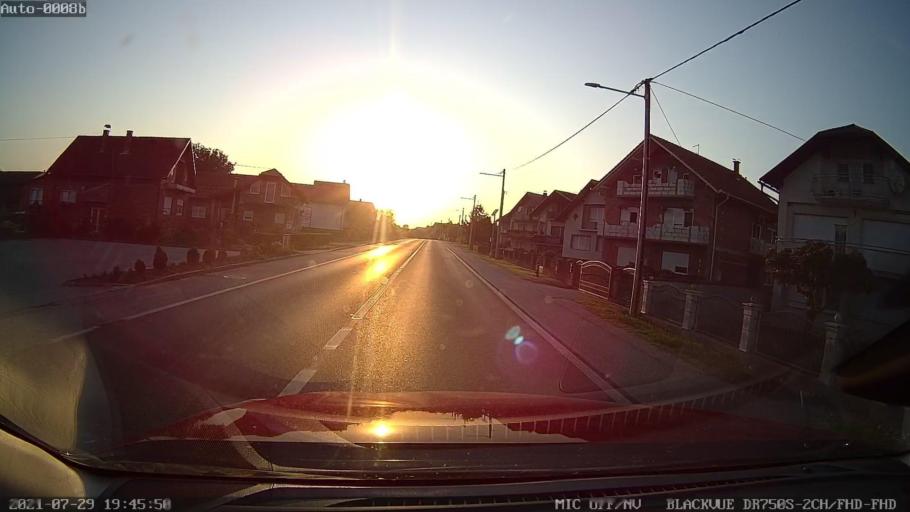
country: HR
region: Varazdinska
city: Ludbreg
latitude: 46.2618
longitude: 16.5816
